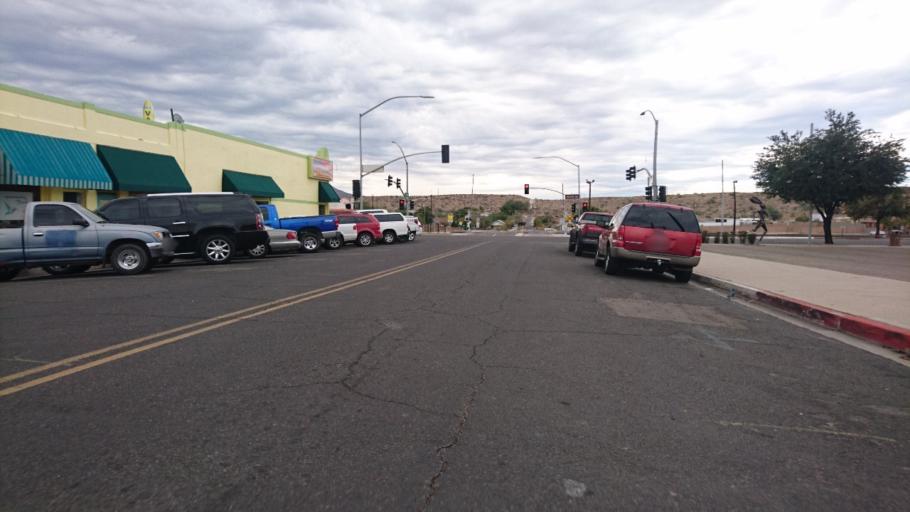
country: US
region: Arizona
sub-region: Mohave County
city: Kingman
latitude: 35.1891
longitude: -114.0531
